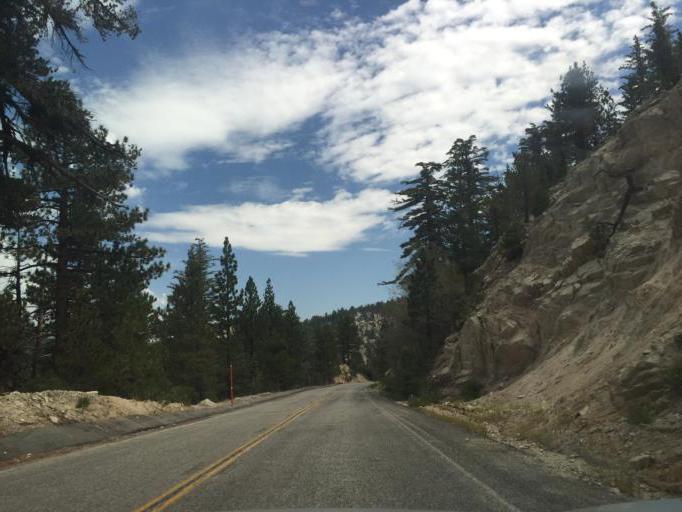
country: US
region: California
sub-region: Los Angeles County
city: Littlerock
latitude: 34.3487
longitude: -117.9232
